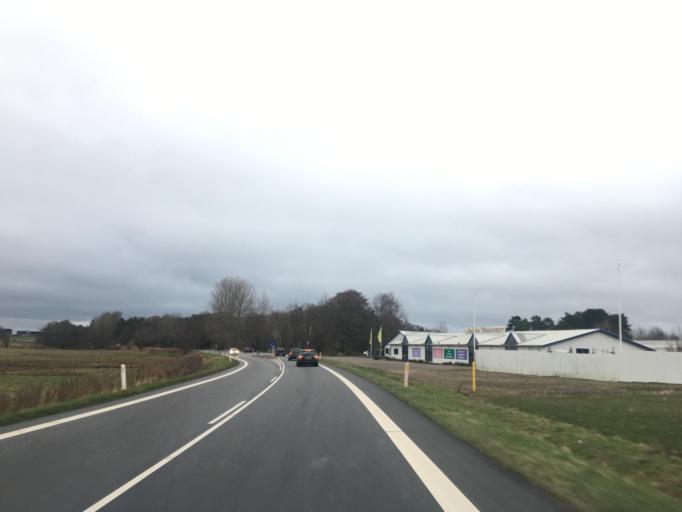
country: DK
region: Zealand
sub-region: Holbaek Kommune
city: Holbaek
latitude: 55.7586
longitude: 11.6277
